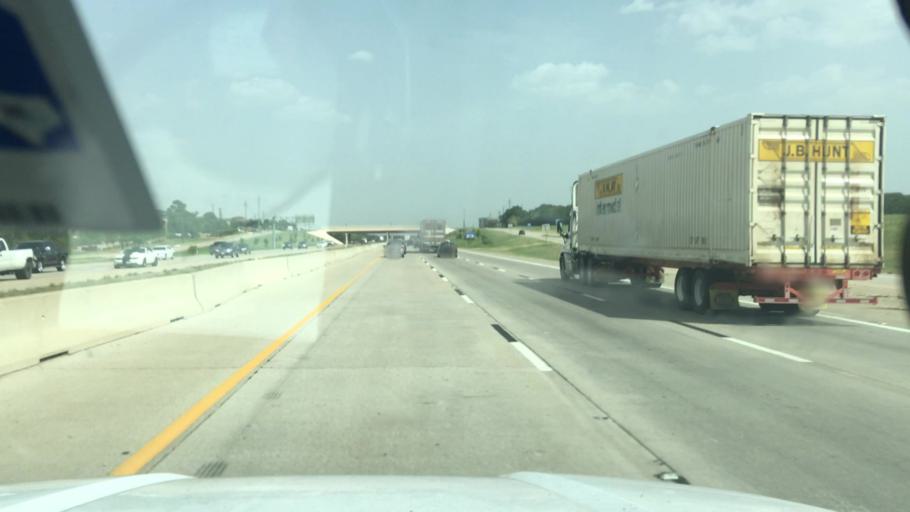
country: US
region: Texas
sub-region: Tarrant County
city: Southlake
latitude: 32.9554
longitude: -97.1393
